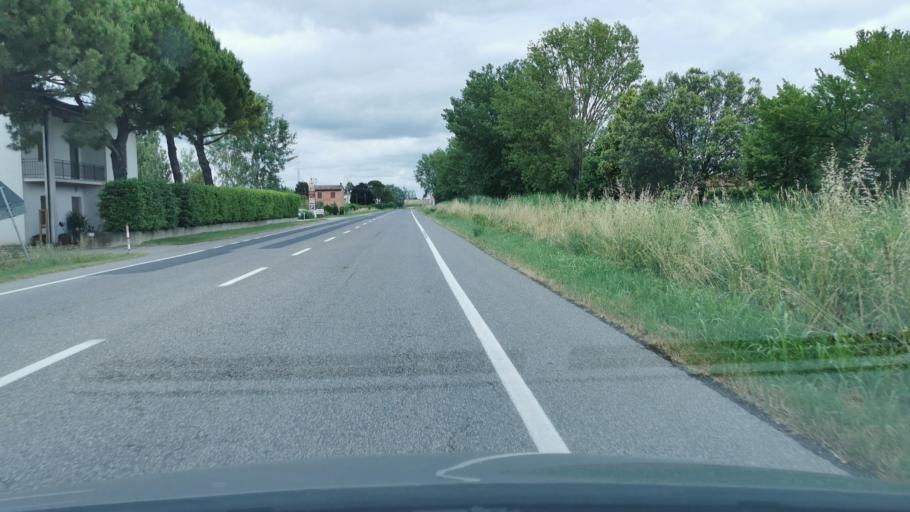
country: IT
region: Emilia-Romagna
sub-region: Provincia di Ravenna
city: Cotignola
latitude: 44.3941
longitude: 11.9580
